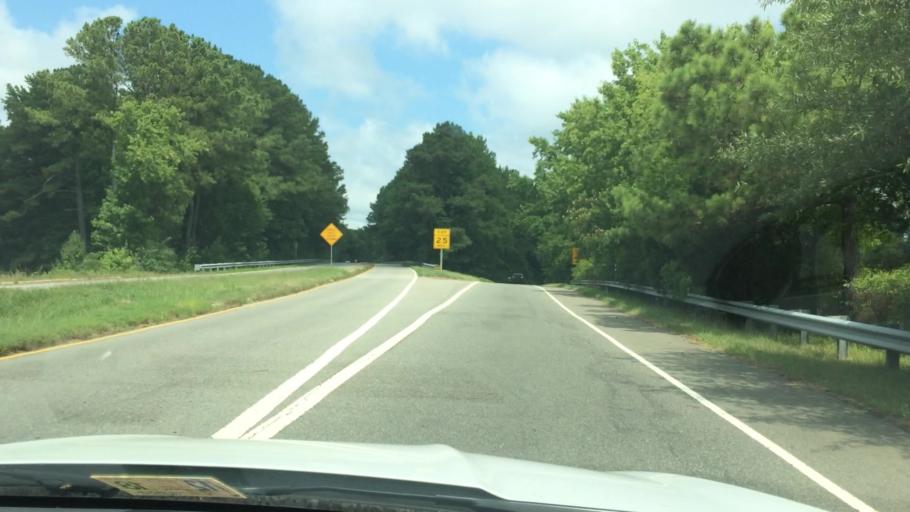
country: US
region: Virginia
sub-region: City of Poquoson
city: Poquoson
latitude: 37.1259
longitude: -76.4568
